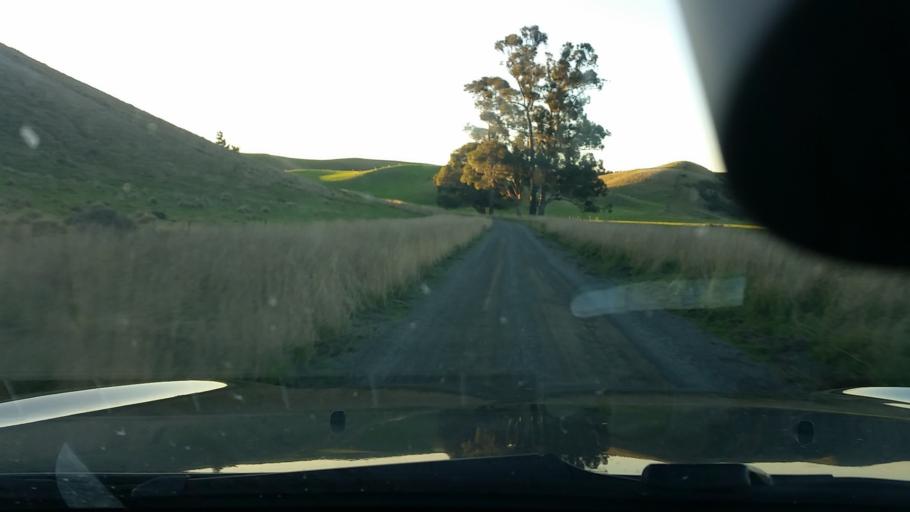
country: NZ
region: Marlborough
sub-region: Marlborough District
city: Blenheim
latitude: -41.7450
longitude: 174.0561
